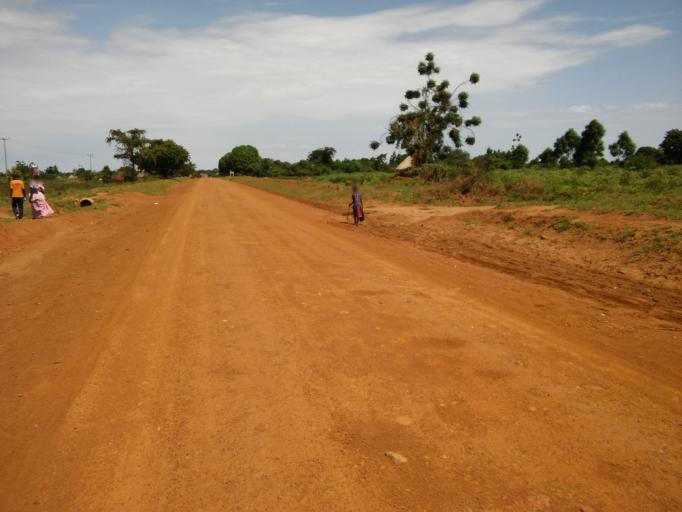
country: UG
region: Eastern Region
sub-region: Kumi District
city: Kumi
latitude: 1.4824
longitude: 33.9047
